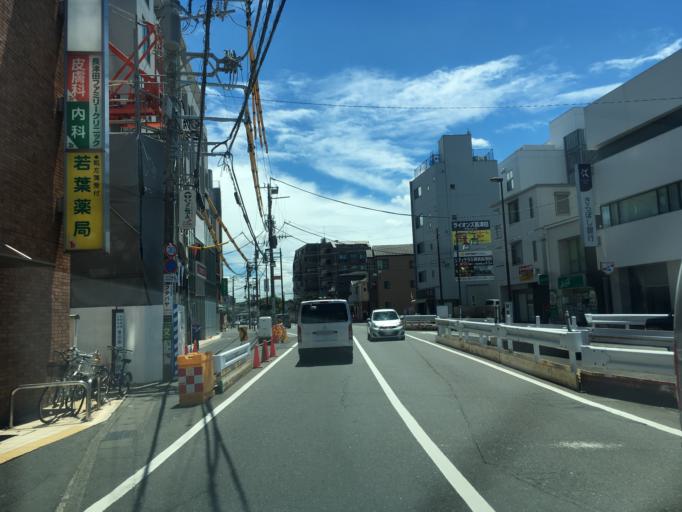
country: JP
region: Tokyo
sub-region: Machida-shi
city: Machida
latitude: 35.5313
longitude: 139.4964
